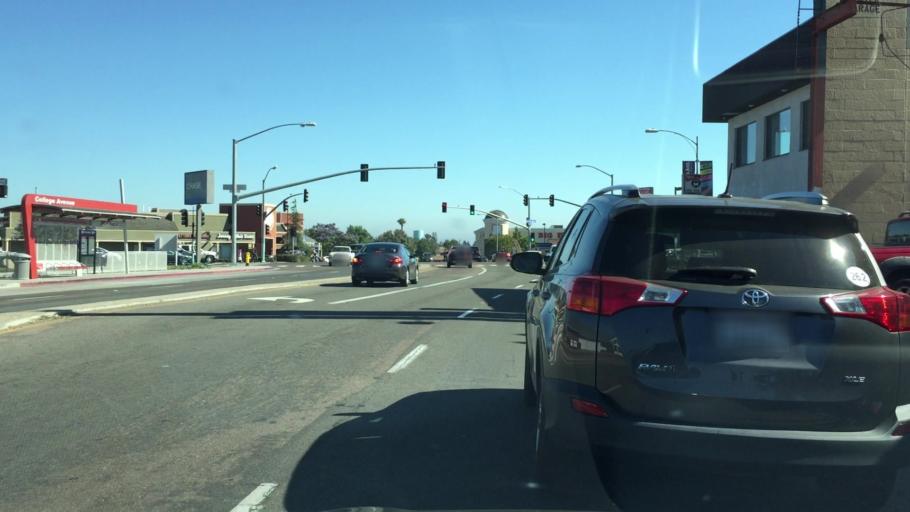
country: US
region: California
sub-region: San Diego County
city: Lemon Grove
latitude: 32.7622
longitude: -117.0670
